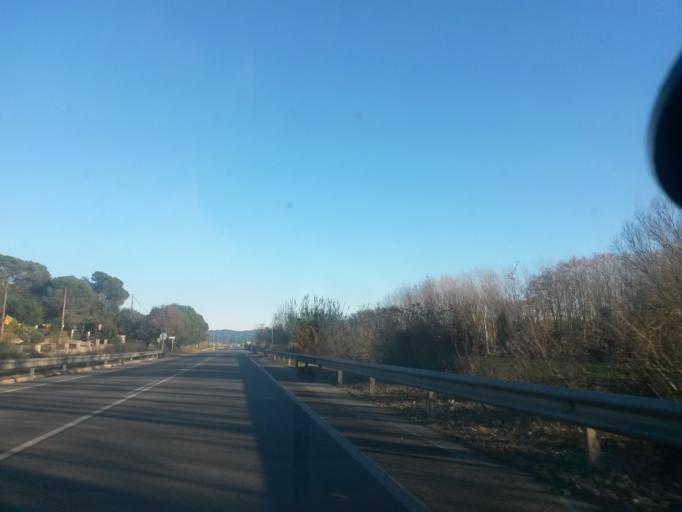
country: ES
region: Catalonia
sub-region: Provincia de Girona
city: Aiguaviva
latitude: 41.9383
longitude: 2.7732
